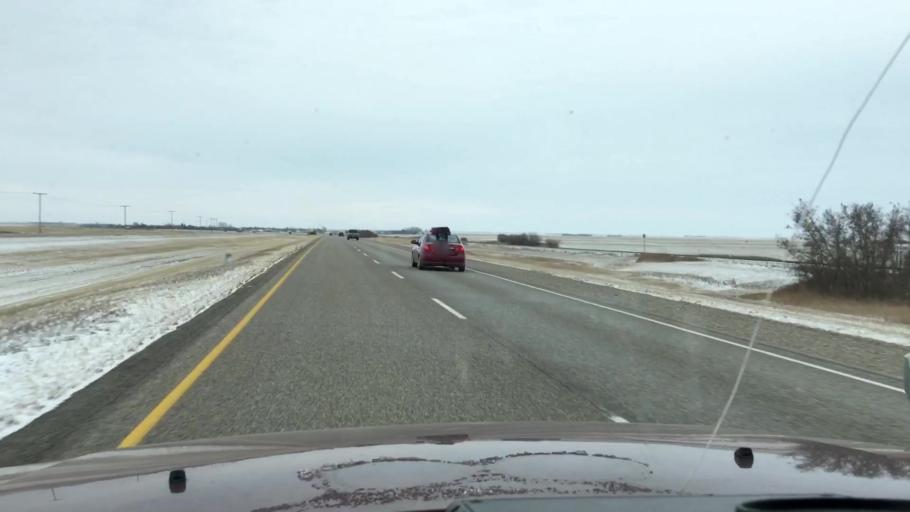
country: CA
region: Saskatchewan
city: Watrous
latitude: 51.1767
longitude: -105.9359
